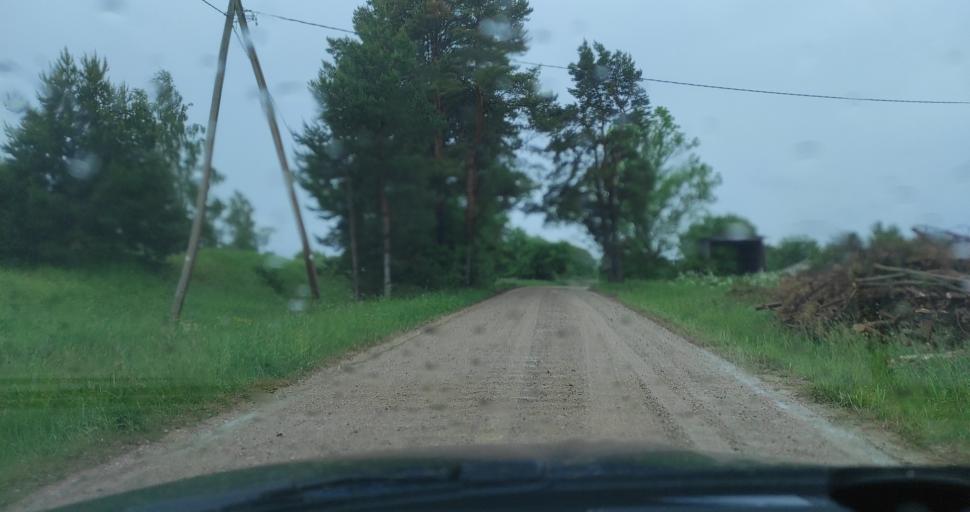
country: LV
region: Alsunga
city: Alsunga
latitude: 56.9993
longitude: 21.3904
